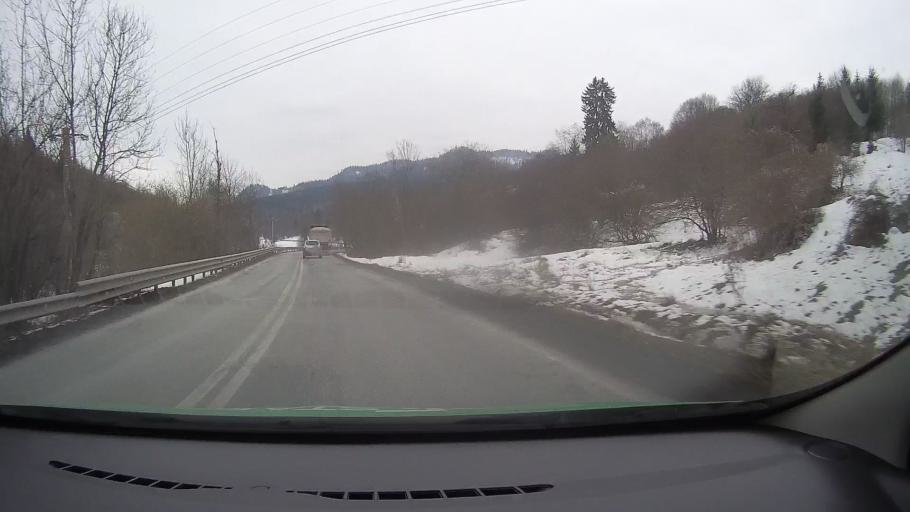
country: RO
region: Brasov
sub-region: Oras Rasnov
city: Rasnov
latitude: 45.5303
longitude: 25.4989
